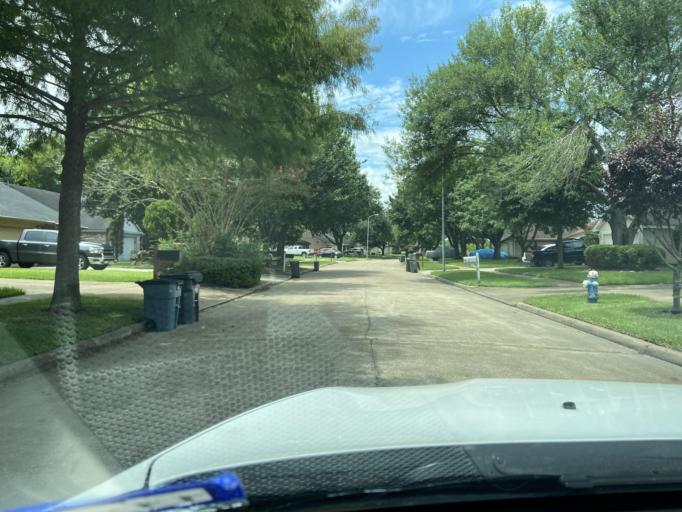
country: US
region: Texas
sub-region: Harris County
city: Jersey Village
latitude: 29.9146
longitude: -95.5759
